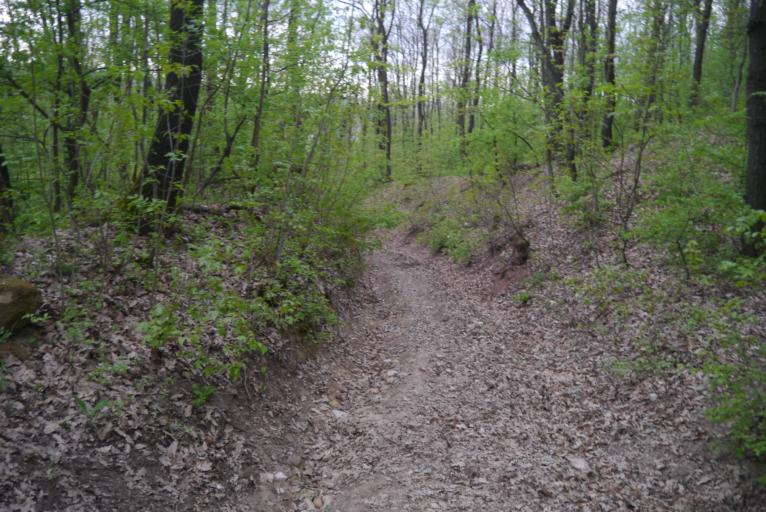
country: HU
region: Komarom-Esztergom
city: Piliscsev
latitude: 47.6824
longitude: 18.8413
